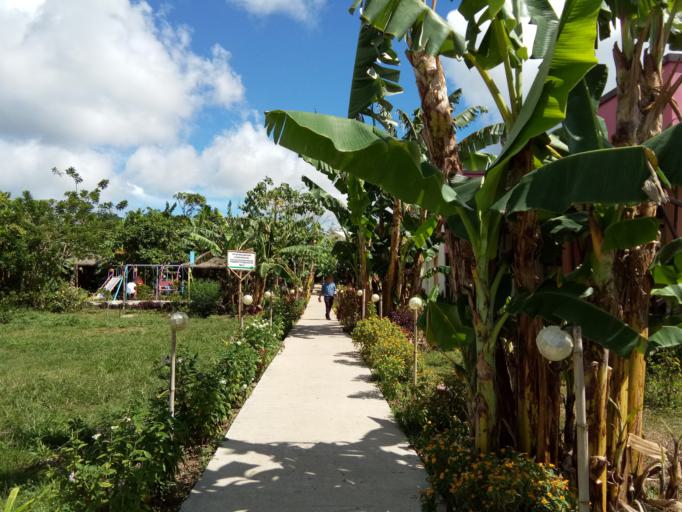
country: PH
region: Calabarzon
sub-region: Province of Cavite
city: Balite Segundo
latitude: 14.1844
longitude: 120.9620
